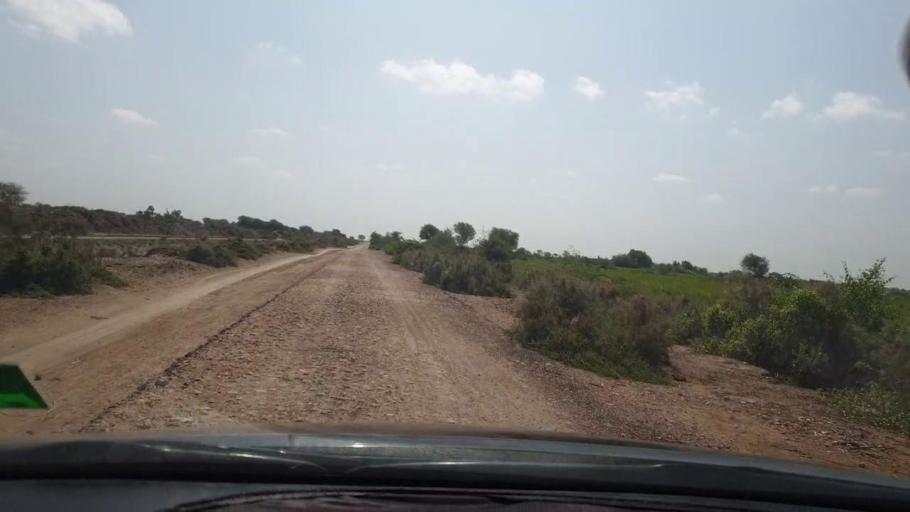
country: PK
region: Sindh
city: Tando Bago
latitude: 24.8442
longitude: 69.0396
